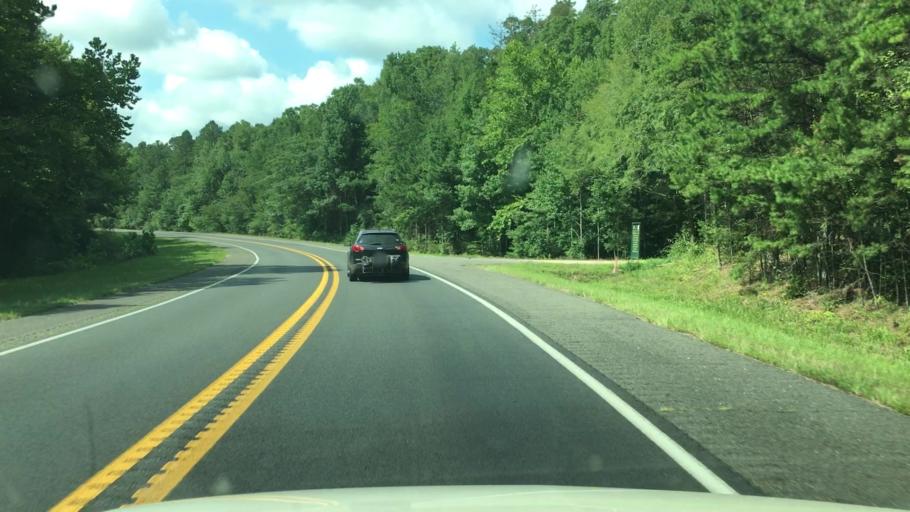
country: US
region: Arkansas
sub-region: Garland County
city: Lake Hamilton
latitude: 34.3531
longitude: -93.1838
